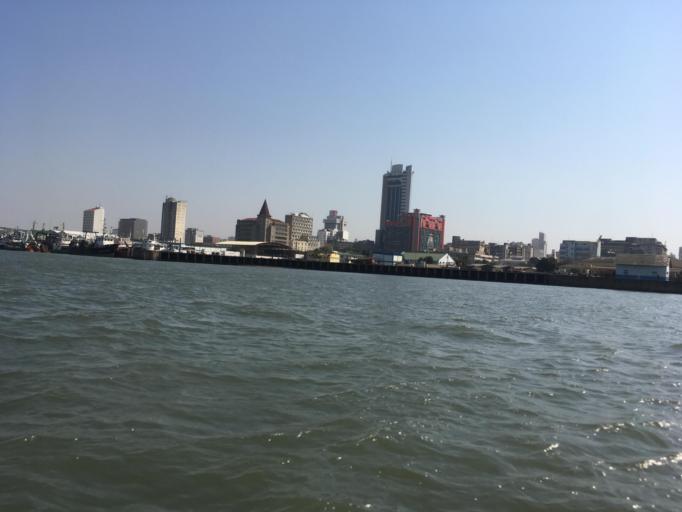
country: MZ
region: Maputo City
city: Maputo
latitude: -25.9795
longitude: 32.5721
